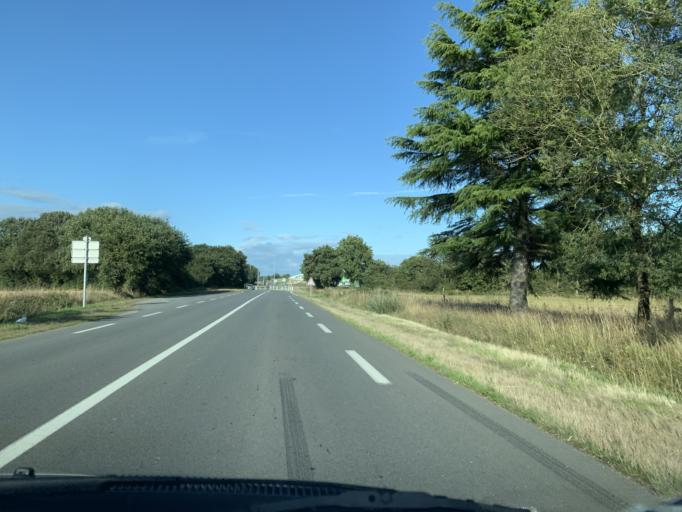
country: FR
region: Brittany
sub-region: Departement du Morbihan
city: Nivillac
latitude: 47.5048
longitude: -2.3035
